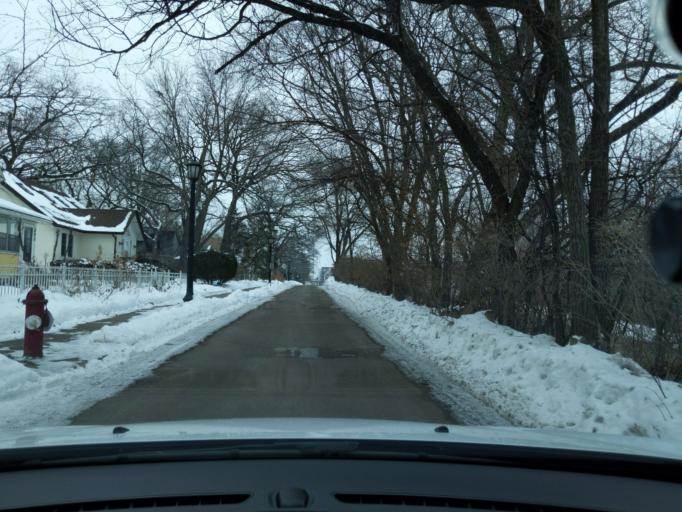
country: US
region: Minnesota
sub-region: Ramsey County
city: Lauderdale
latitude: 44.9605
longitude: -93.2079
